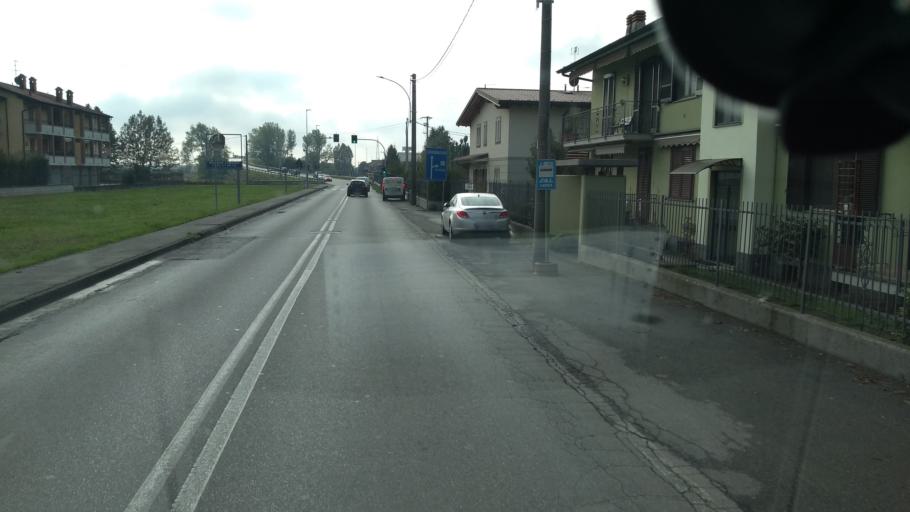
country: IT
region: Lombardy
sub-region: Provincia di Bergamo
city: Vidalengo
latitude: 45.5213
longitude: 9.6399
